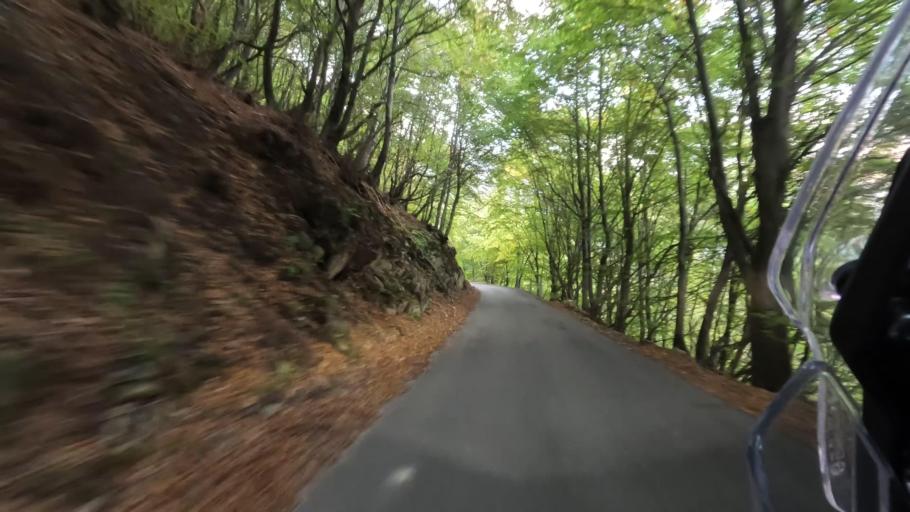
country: IT
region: Lombardy
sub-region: Provincia di Como
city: Pigra
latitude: 45.9638
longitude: 9.1234
